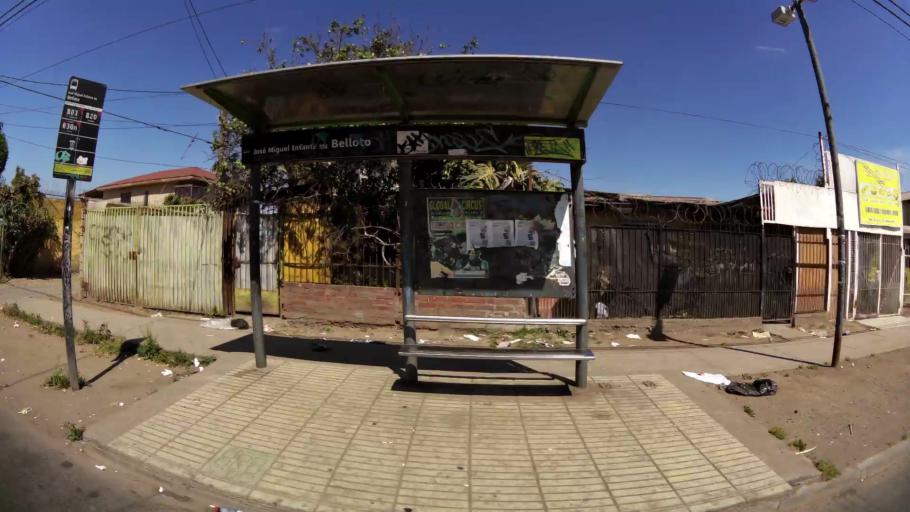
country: CL
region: Santiago Metropolitan
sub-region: Provincia de Santiago
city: Lo Prado
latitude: -33.4066
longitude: -70.7257
